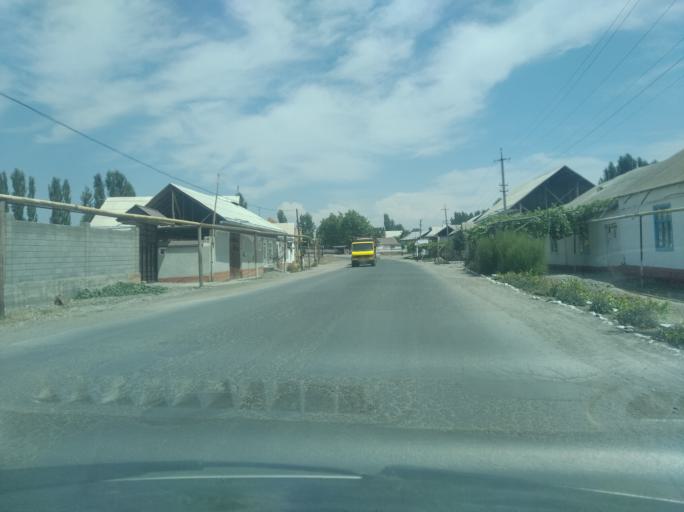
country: UZ
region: Andijon
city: Khujaobod
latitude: 40.6277
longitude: 72.4509
